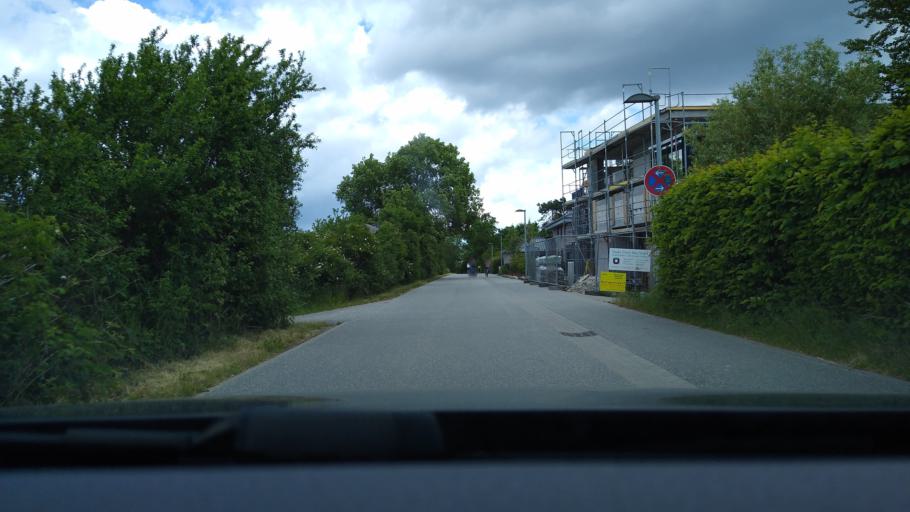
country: DE
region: Schleswig-Holstein
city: Dahme
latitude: 54.2087
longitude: 11.0895
